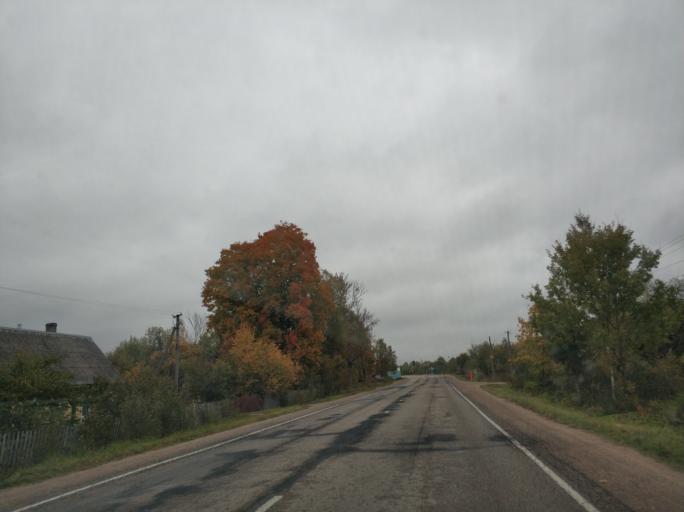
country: BY
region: Vitebsk
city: Rasony
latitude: 56.0544
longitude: 28.7117
